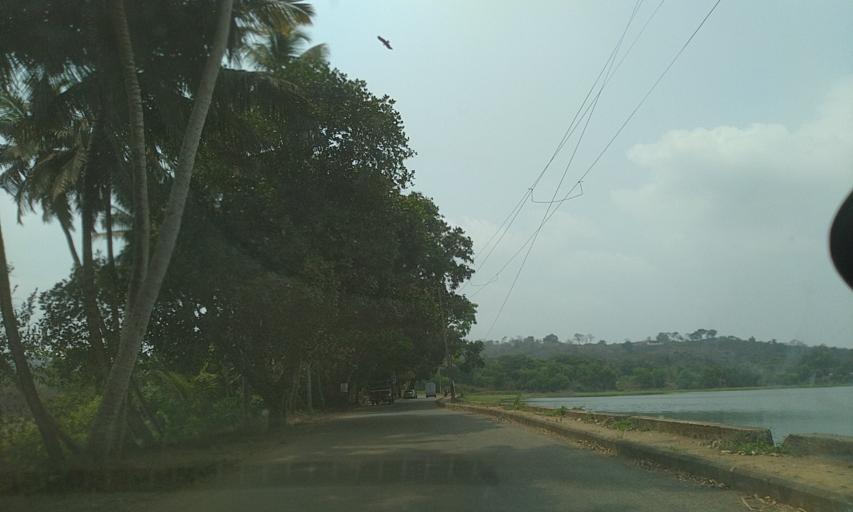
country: IN
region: Goa
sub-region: North Goa
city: Jua
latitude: 15.4863
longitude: 73.9277
